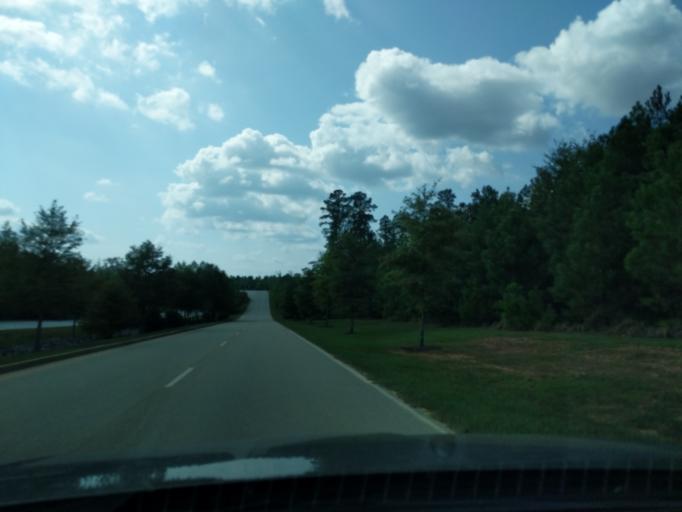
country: US
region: Georgia
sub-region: Columbia County
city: Grovetown
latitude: 33.4795
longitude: -82.1874
